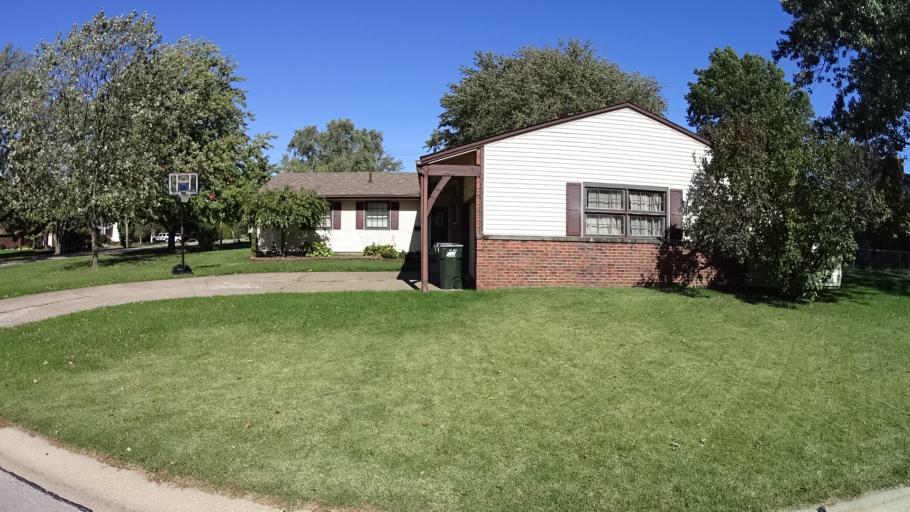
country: US
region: Ohio
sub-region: Lorain County
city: Amherst
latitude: 41.4066
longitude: -82.2286
